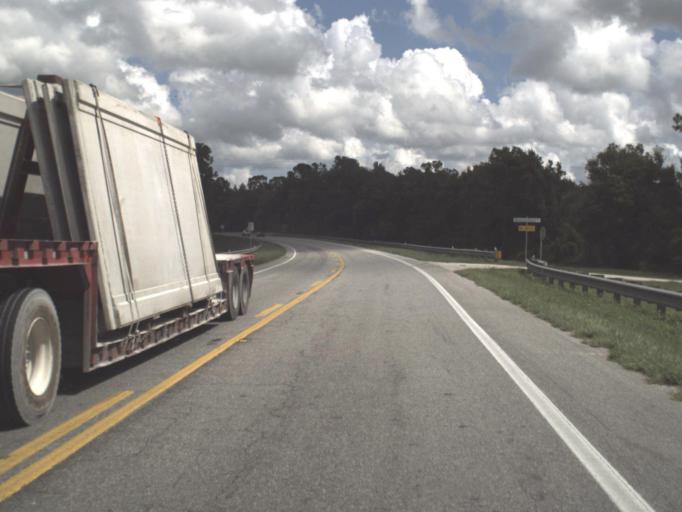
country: US
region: Florida
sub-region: Lake County
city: Four Corners
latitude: 28.3580
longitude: -81.8199
